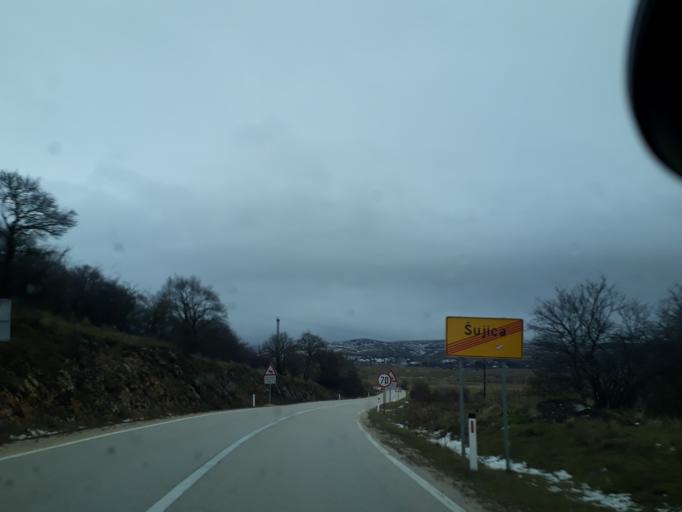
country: BA
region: Federation of Bosnia and Herzegovina
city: Tomislavgrad
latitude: 43.8356
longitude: 17.1874
